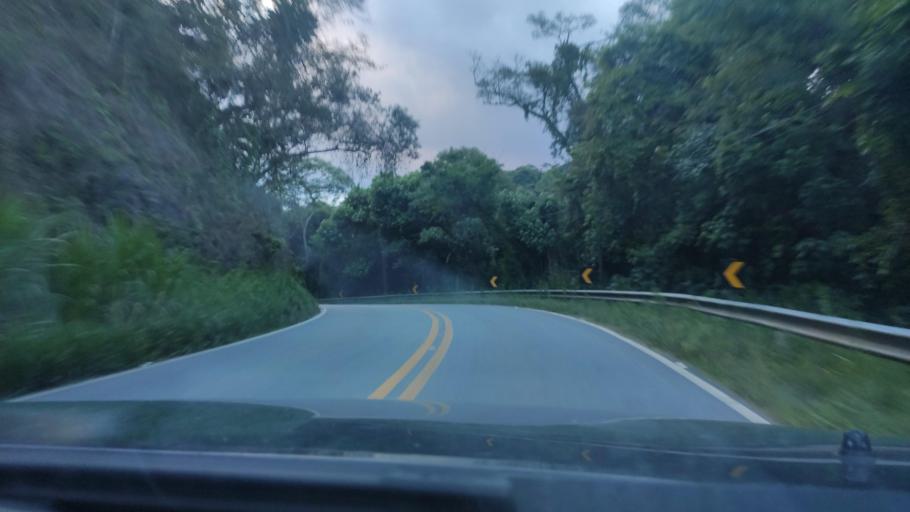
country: BR
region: Sao Paulo
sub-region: Campos Do Jordao
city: Campos do Jordao
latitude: -22.8258
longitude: -45.6789
